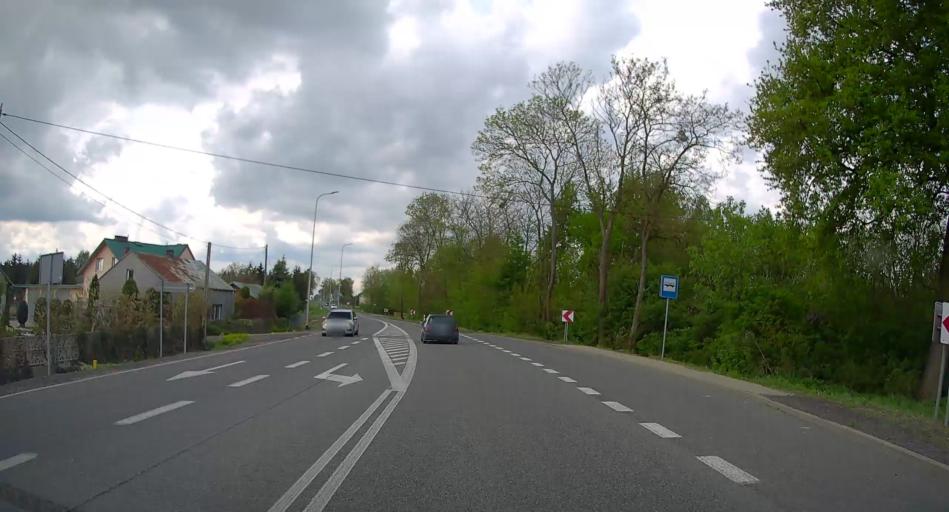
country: PL
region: Masovian Voivodeship
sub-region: Powiat plonski
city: Zaluski
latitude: 52.4467
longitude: 20.5000
